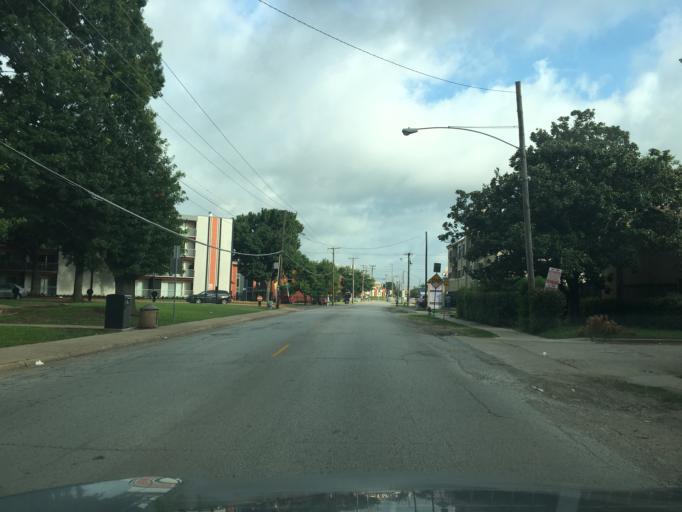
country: US
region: Texas
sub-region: Dallas County
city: University Park
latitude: 32.8696
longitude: -96.7583
